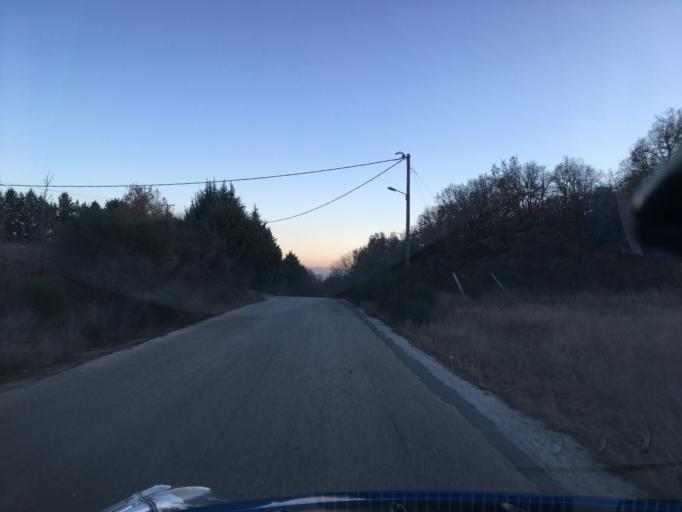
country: GR
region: West Macedonia
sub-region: Nomos Kozanis
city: Kozani
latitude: 40.2622
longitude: 21.7487
